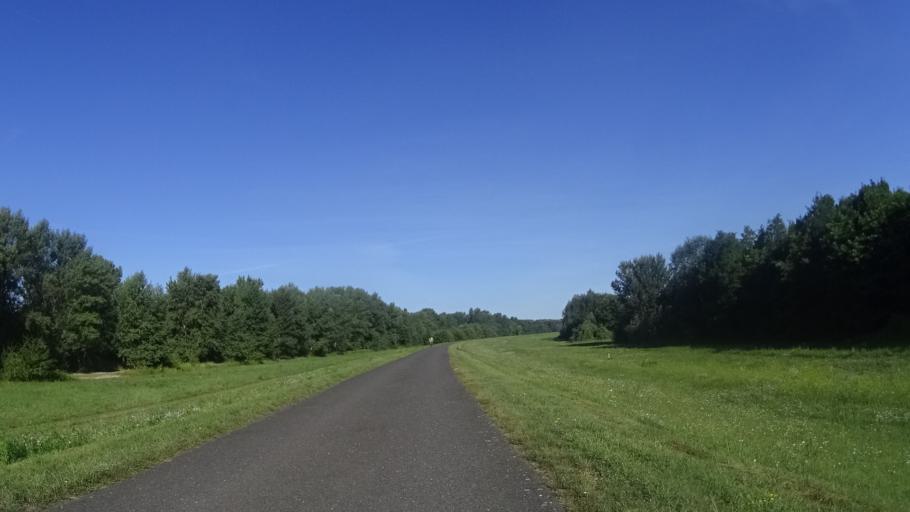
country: HU
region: Gyor-Moson-Sopron
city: Rajka
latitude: 48.0650
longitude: 17.1760
